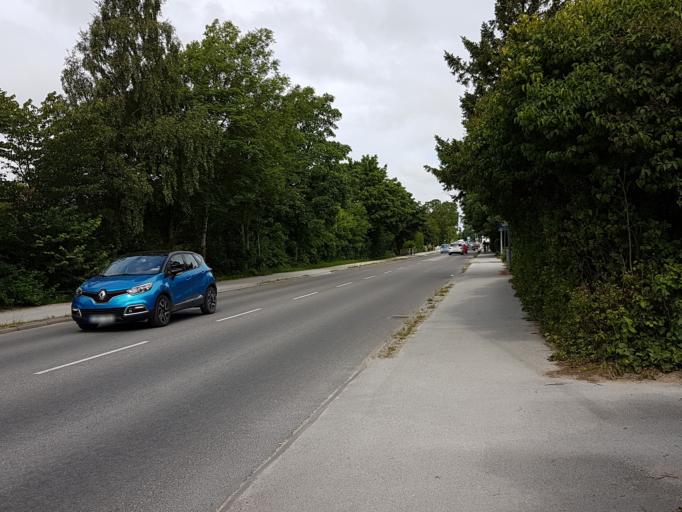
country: SE
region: Gotland
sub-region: Gotland
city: Visby
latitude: 57.6288
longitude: 18.3167
